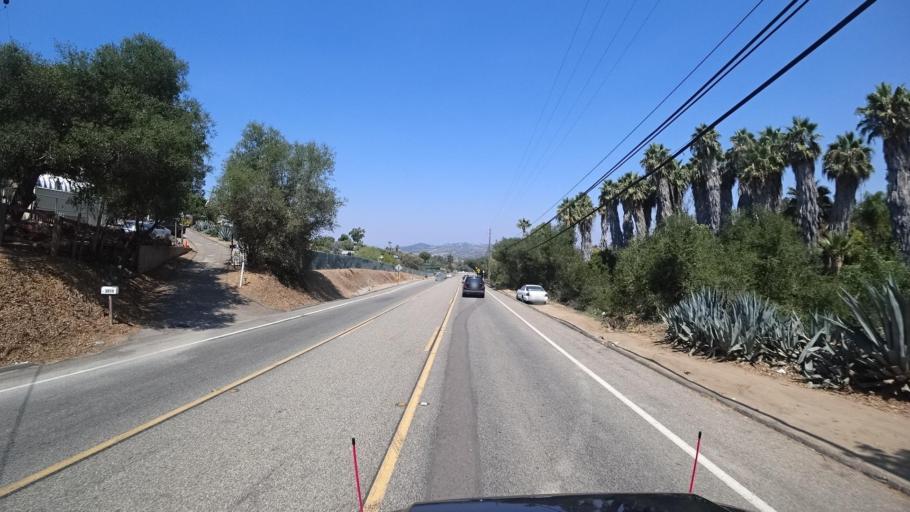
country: US
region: California
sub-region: San Diego County
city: Bonsall
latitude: 33.2487
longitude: -117.2291
